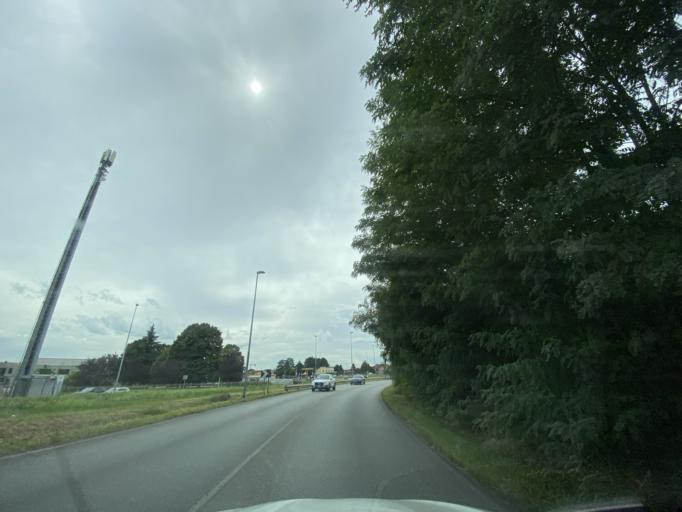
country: IT
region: Lombardy
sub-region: Citta metropolitana di Milano
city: Pessano Con Bornago
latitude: 45.5439
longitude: 9.3934
